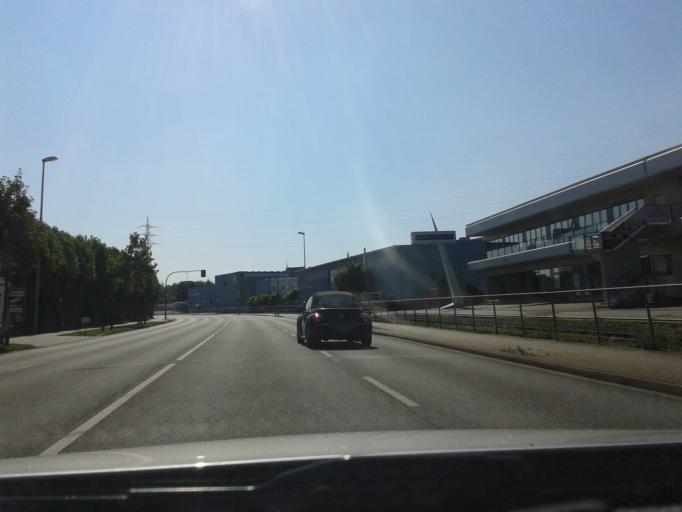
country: DE
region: North Rhine-Westphalia
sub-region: Regierungsbezirk Dusseldorf
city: Muelheim (Ruhr)
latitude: 51.4305
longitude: 6.8520
